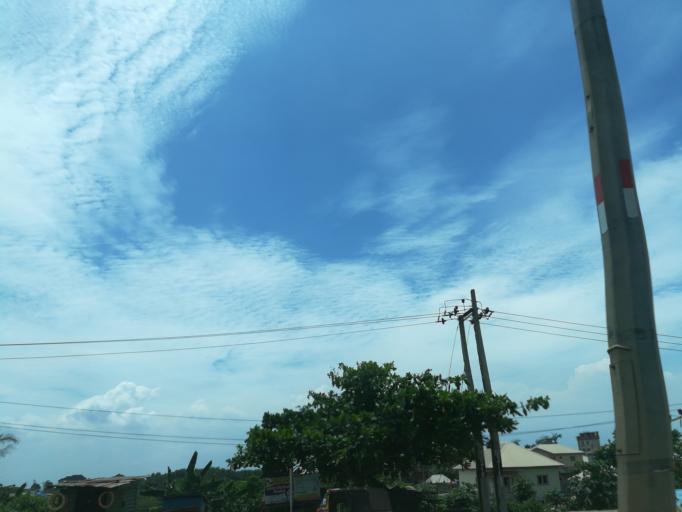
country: NG
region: Lagos
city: Ebute Ikorodu
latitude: 6.5955
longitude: 3.4935
